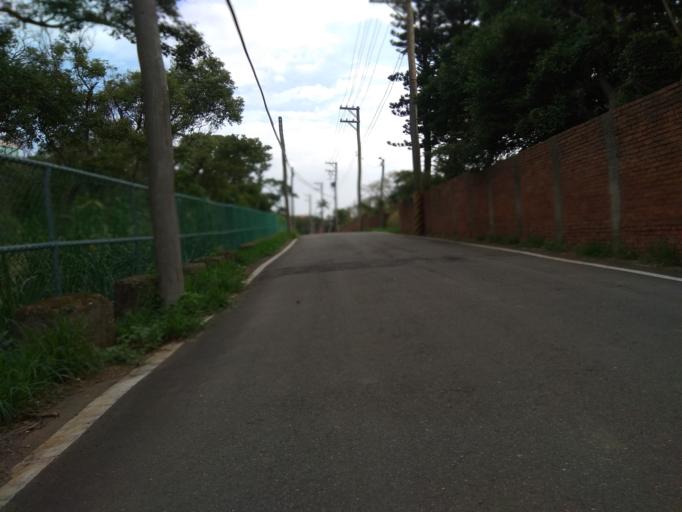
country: TW
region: Taiwan
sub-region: Hsinchu
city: Zhubei
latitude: 24.9742
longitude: 121.0247
